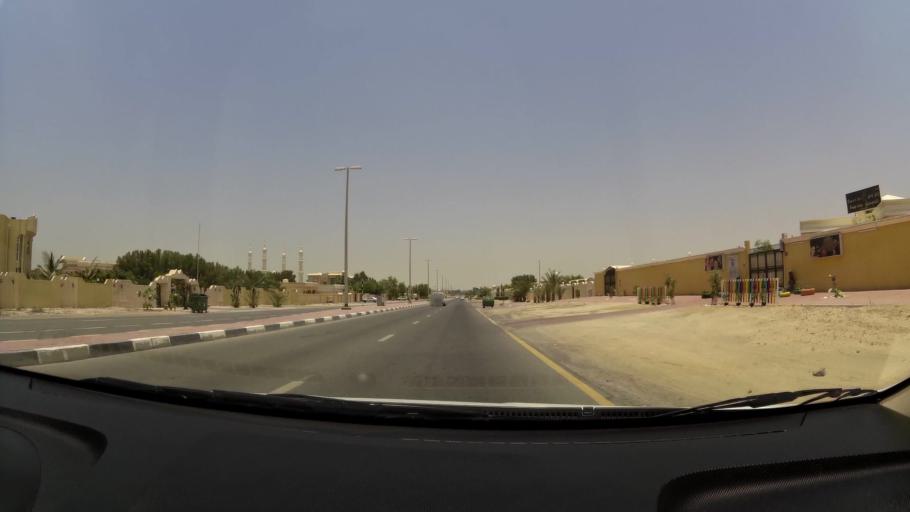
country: AE
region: Ajman
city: Ajman
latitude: 25.4127
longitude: 55.4881
